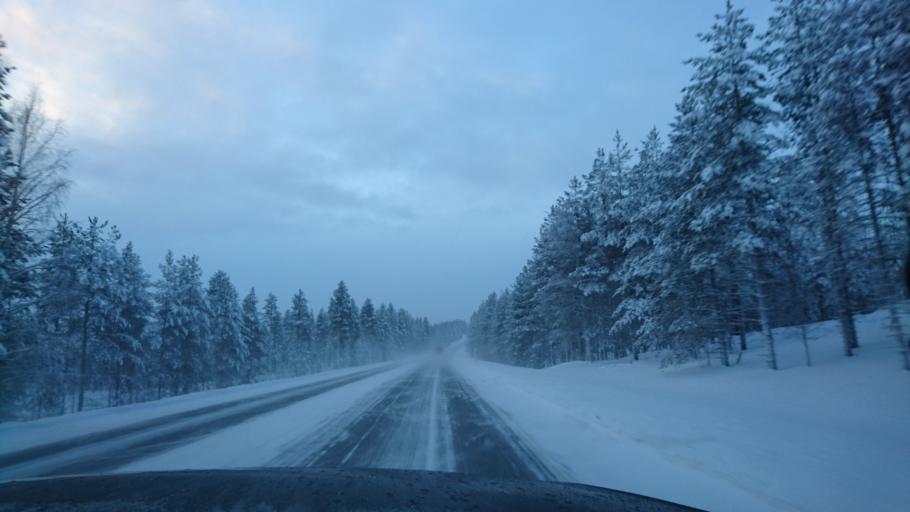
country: FI
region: Kainuu
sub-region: Kehys-Kainuu
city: Puolanka
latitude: 65.4427
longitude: 27.6111
